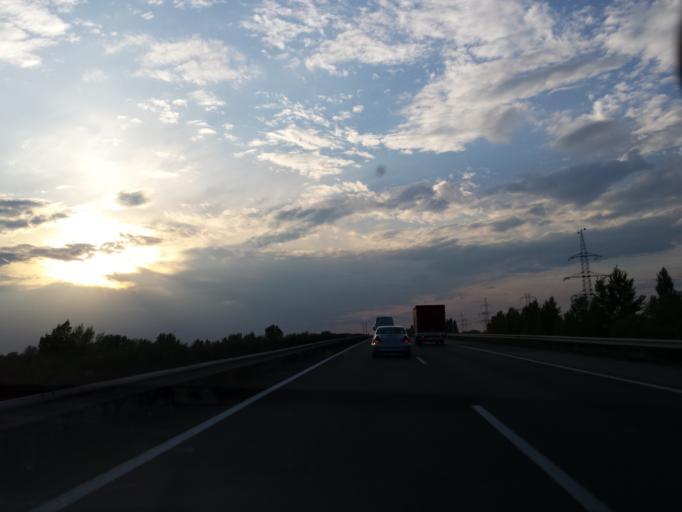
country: HU
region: Gyor-Moson-Sopron
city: Abda
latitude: 47.6644
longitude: 17.5773
